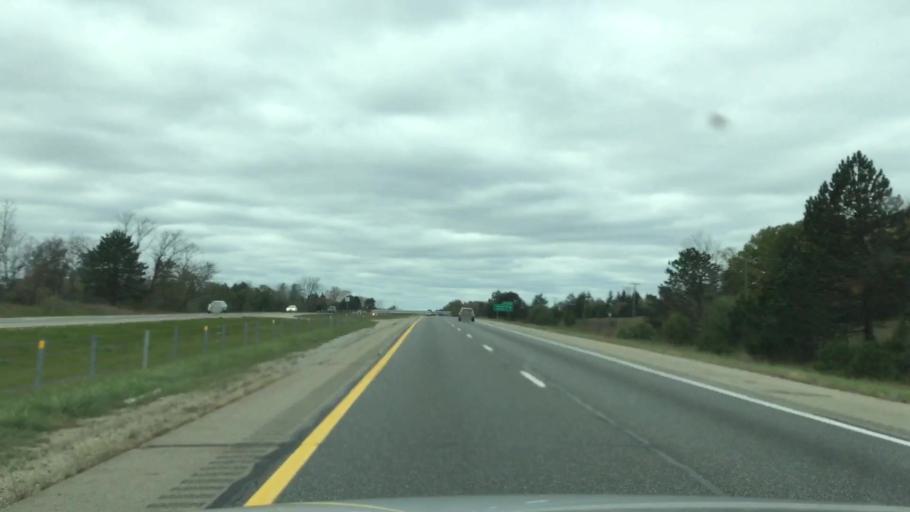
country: US
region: Michigan
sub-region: Washtenaw County
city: Chelsea
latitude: 42.2986
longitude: -83.9648
